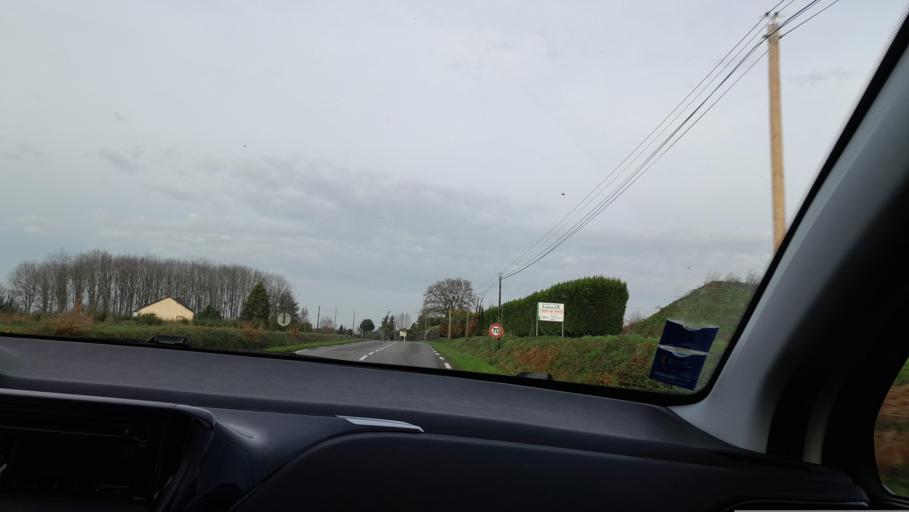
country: FR
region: Brittany
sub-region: Departement d'Ille-et-Vilaine
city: La Guerche-de-Bretagne
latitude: 47.9171
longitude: -1.2067
